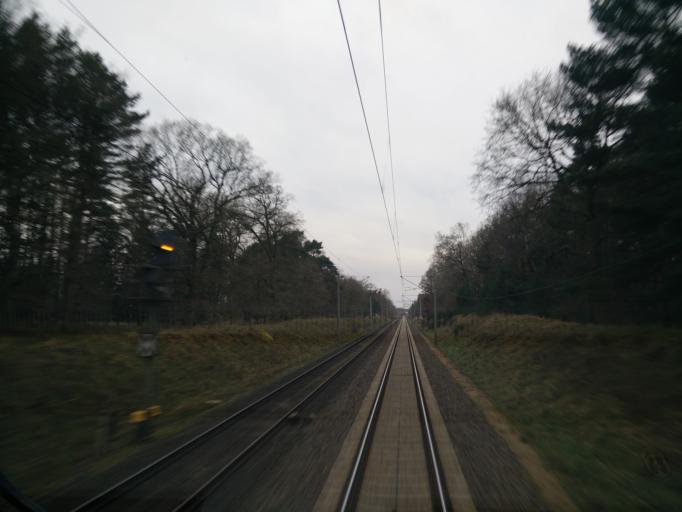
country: DE
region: Mecklenburg-Vorpommern
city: Grabow
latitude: 53.2728
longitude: 11.5843
